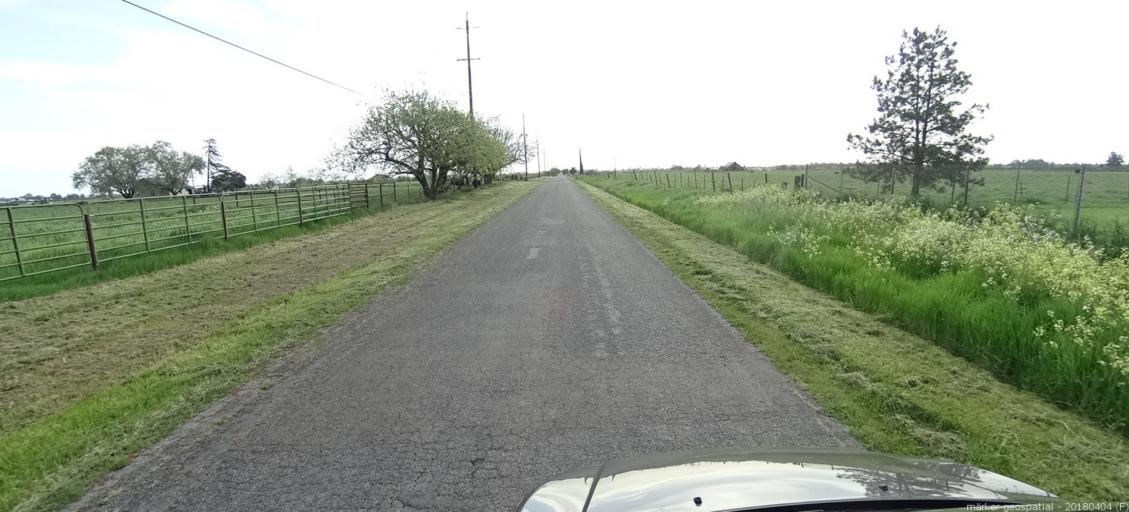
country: US
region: California
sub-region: Sacramento County
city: Galt
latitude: 38.3026
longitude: -121.3157
